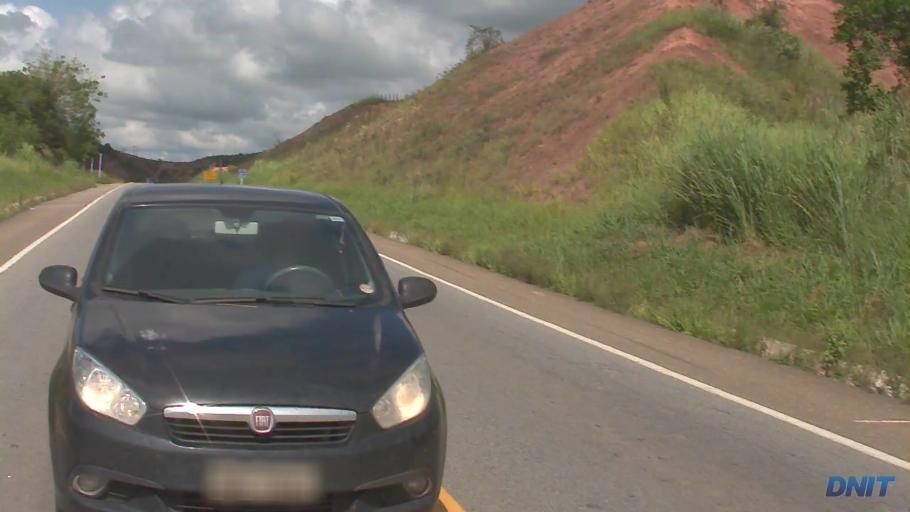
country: BR
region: Minas Gerais
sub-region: Belo Oriente
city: Belo Oriente
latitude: -19.1447
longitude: -42.2287
